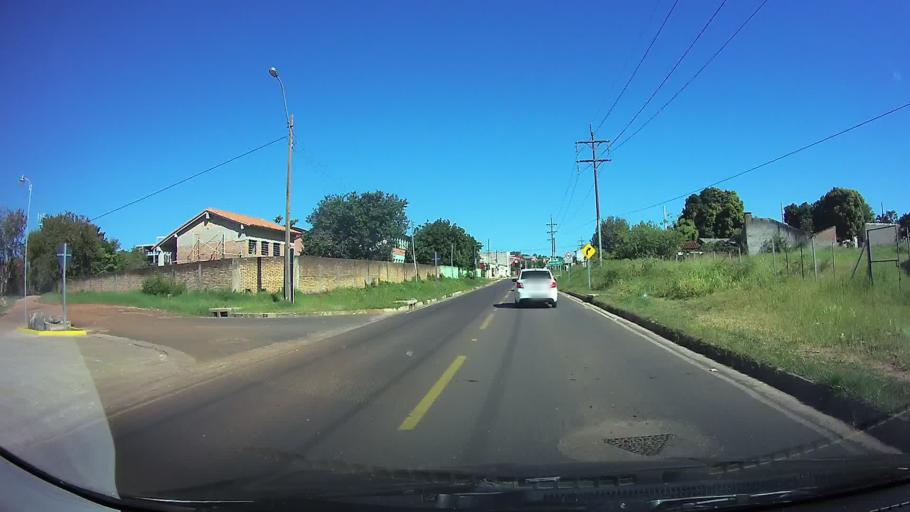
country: PY
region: Central
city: Fernando de la Mora
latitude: -25.3032
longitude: -57.5321
